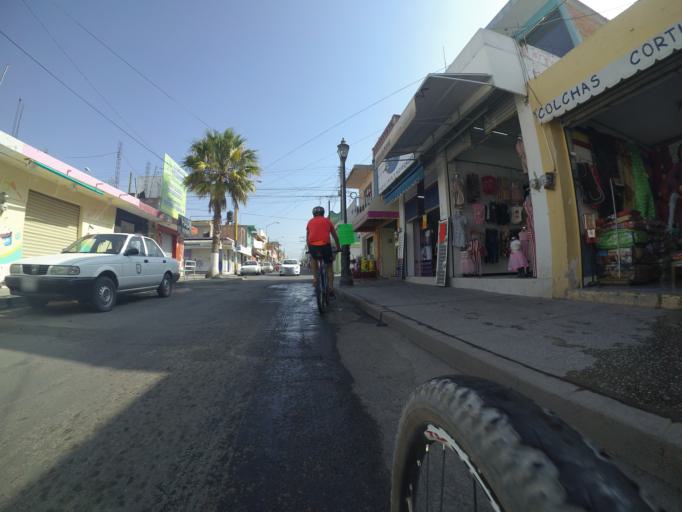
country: MX
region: Aguascalientes
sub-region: Jesus Maria
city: Jesus Maria
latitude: 21.9630
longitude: -102.3432
